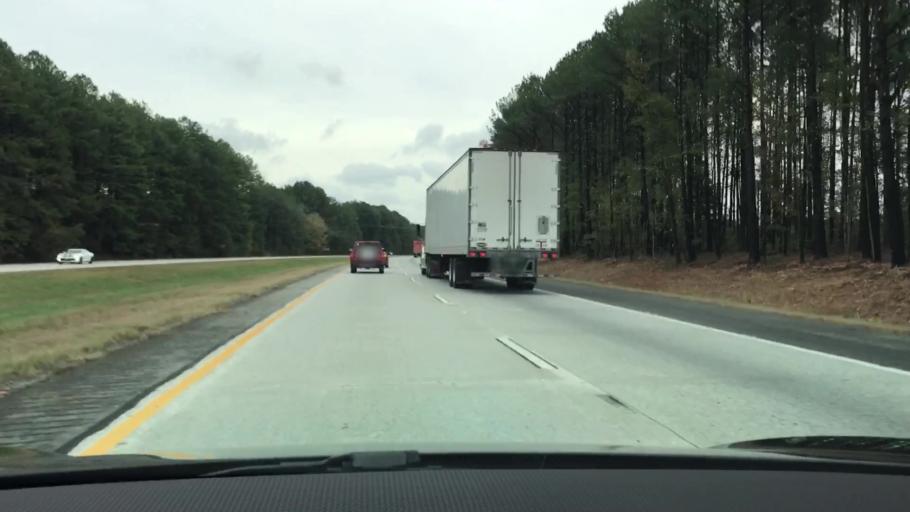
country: US
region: Georgia
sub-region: Taliaferro County
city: Crawfordville
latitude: 33.5302
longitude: -82.9315
